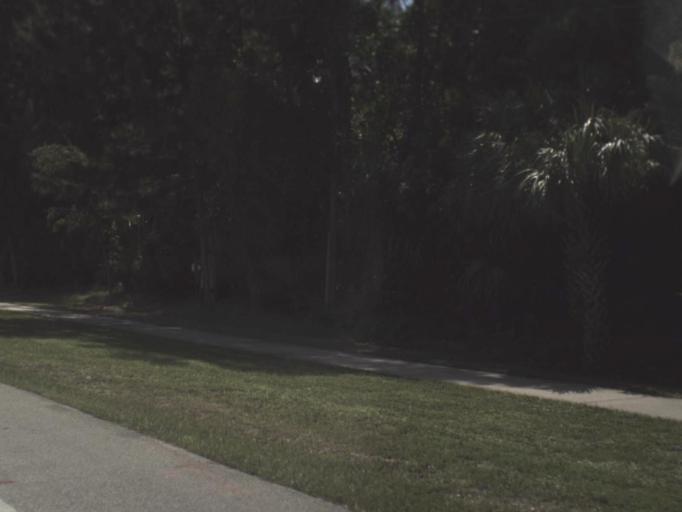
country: US
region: Florida
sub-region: Collier County
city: Naples Manor
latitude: 26.0864
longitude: -81.7292
